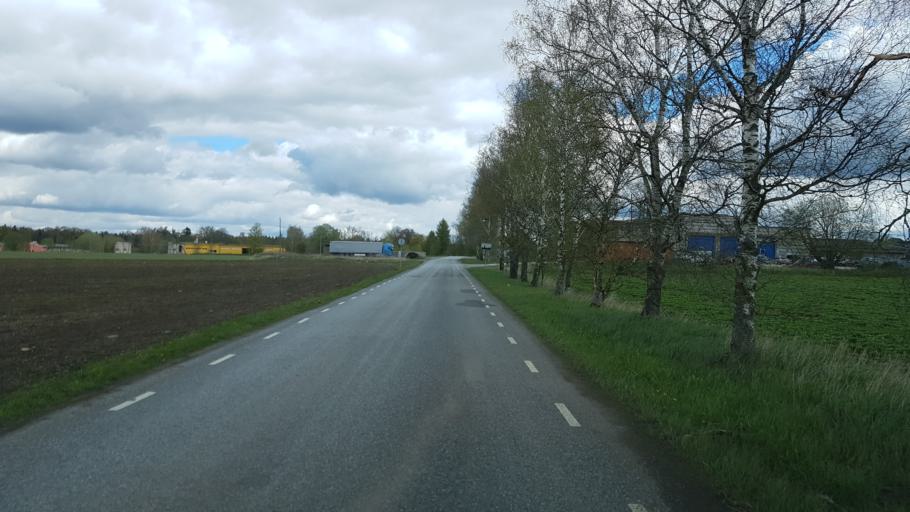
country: EE
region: Raplamaa
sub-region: Kehtna vald
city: Kehtna
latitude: 58.9567
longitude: 24.8355
